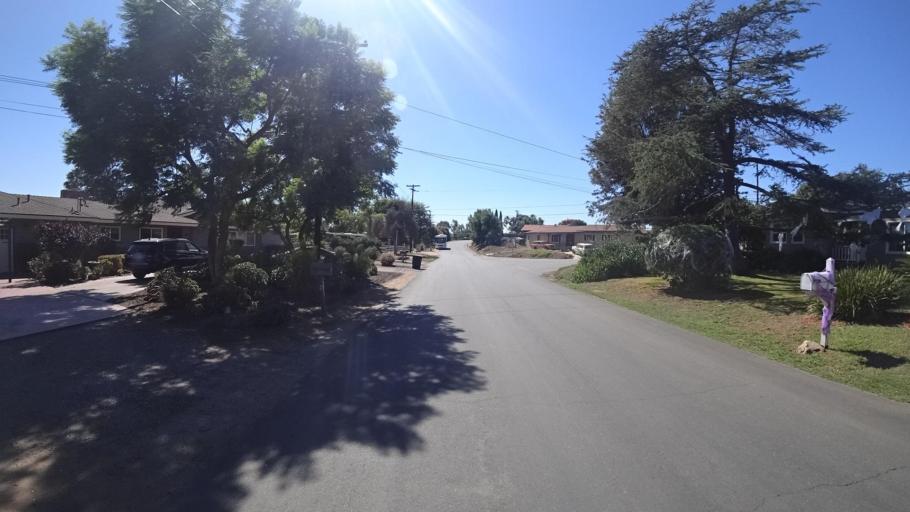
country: US
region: California
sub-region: San Diego County
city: Bonita
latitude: 32.6535
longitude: -117.0547
